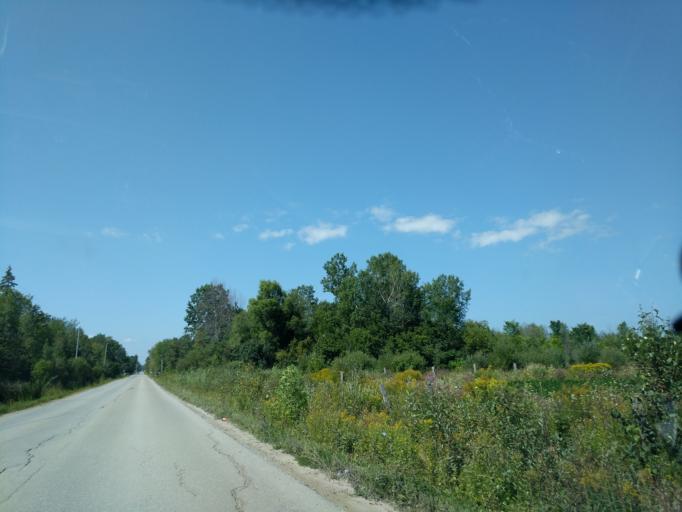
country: CA
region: Ontario
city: Bells Corners
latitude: 45.4474
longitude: -75.9045
